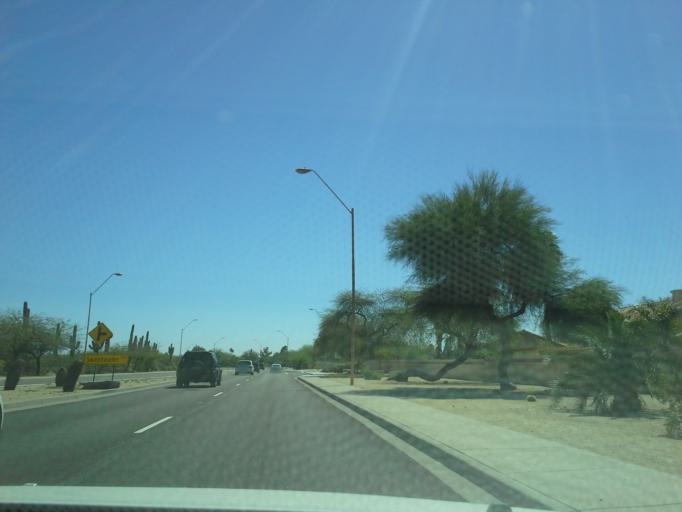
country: US
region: Arizona
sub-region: Maricopa County
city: Scottsdale
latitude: 33.6057
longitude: -111.8556
